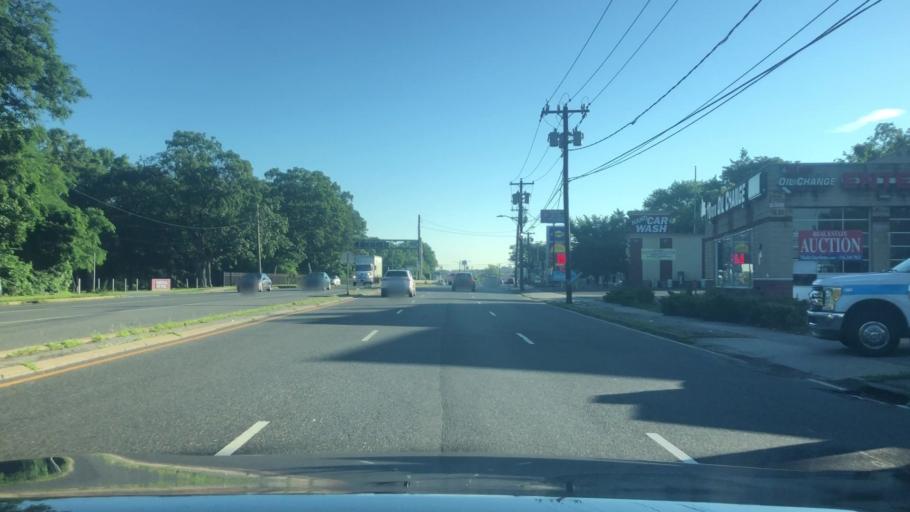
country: US
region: New York
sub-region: Nassau County
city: Hempstead
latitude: 40.6950
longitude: -73.6310
